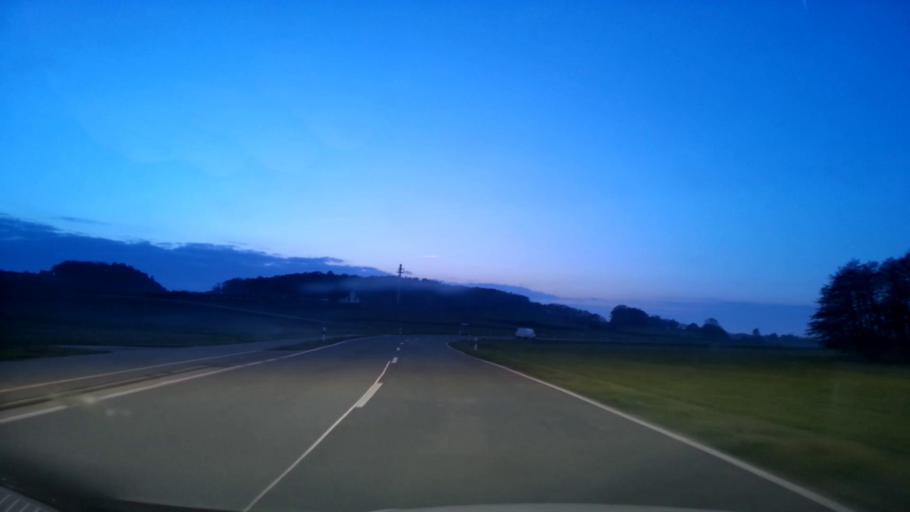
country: DE
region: Bavaria
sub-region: Upper Franconia
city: Frensdorf
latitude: 49.8489
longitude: 10.8913
